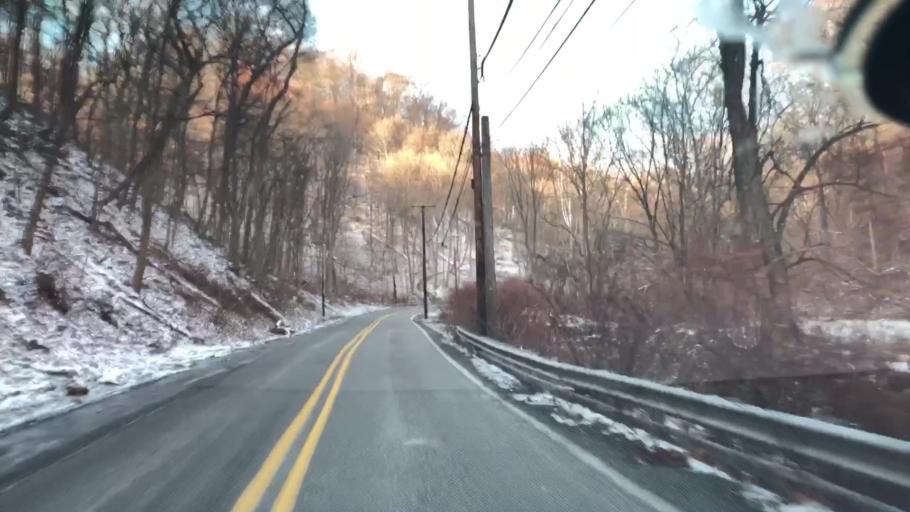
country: US
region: Pennsylvania
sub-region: Allegheny County
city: Penn Hills
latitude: 40.4738
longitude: -79.8379
